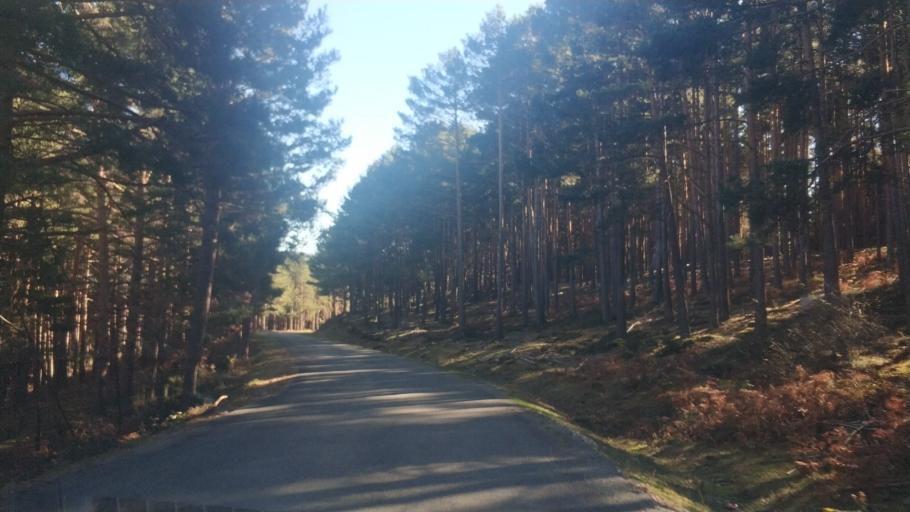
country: ES
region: Castille and Leon
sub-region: Provincia de Soria
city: Vinuesa
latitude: 41.9684
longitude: -2.7925
